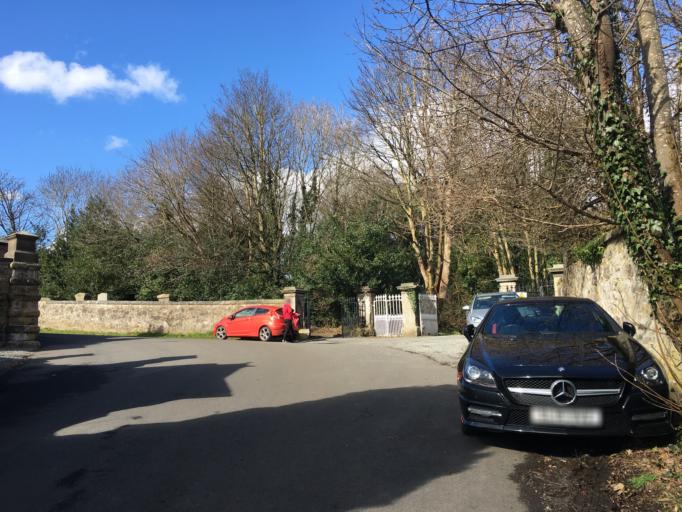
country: GB
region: Scotland
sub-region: Midlothian
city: Bonnyrigg
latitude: 55.8828
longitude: -3.1181
